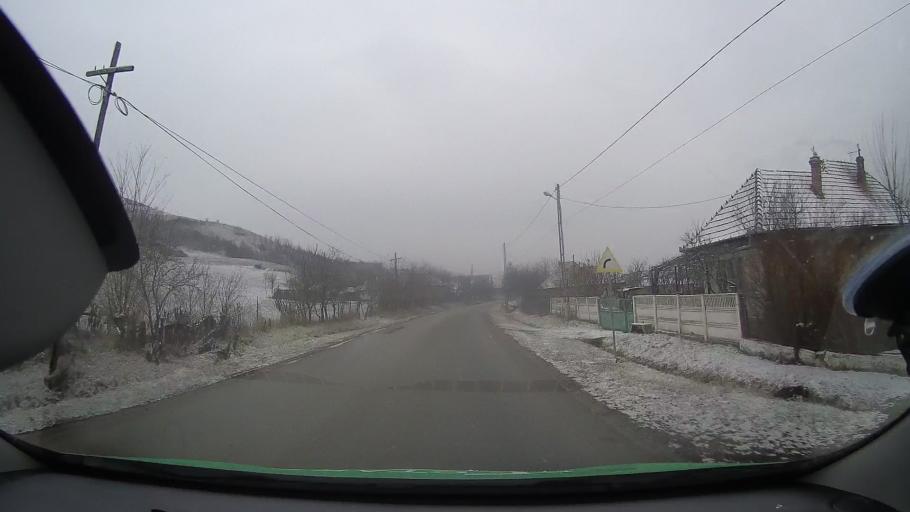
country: RO
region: Alba
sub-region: Comuna Noslac
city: Noslac
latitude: 46.3485
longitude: 23.9383
